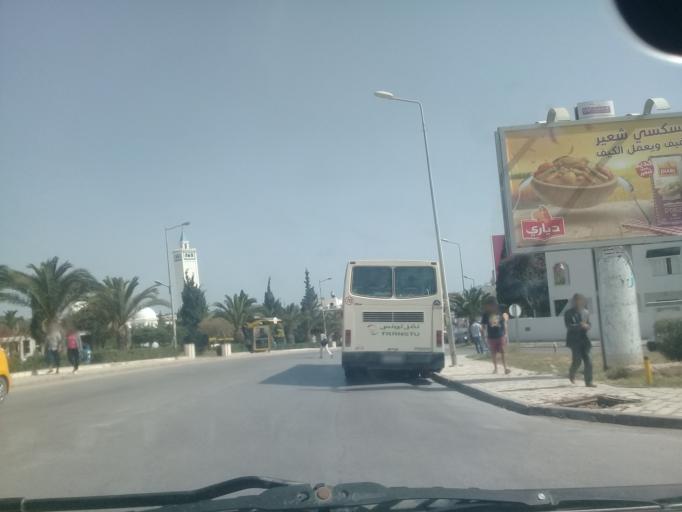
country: TN
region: Tunis
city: Al Marsa
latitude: 36.8891
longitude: 10.3223
